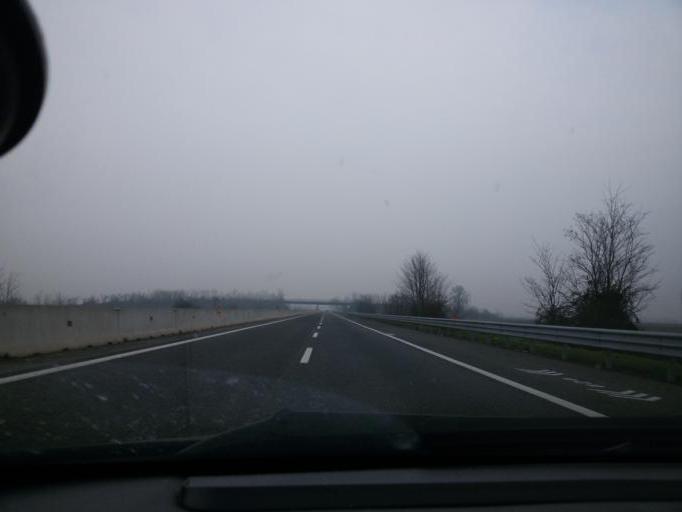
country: IT
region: Piedmont
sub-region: Provincia di Vercelli
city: Asigliano Vercellese
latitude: 45.2749
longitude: 8.4129
